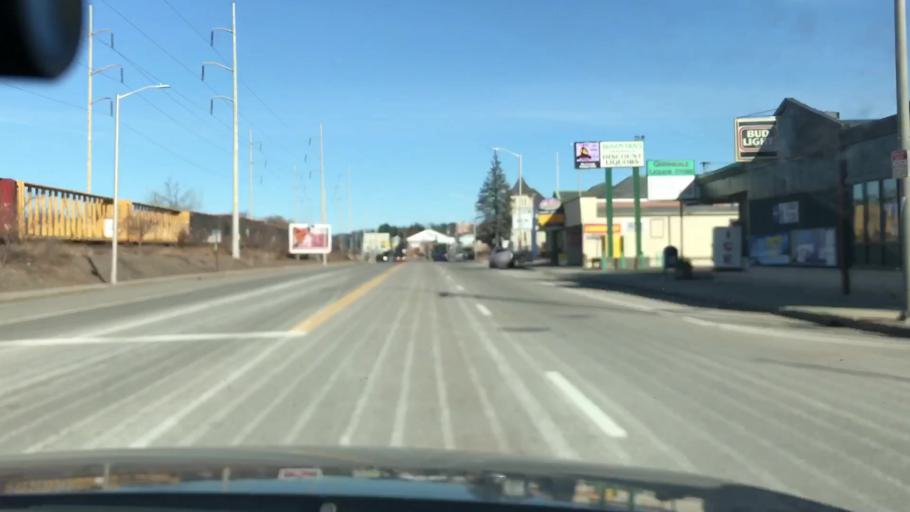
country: US
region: Massachusetts
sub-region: Worcester County
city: Worcester
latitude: 42.3064
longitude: -71.7999
